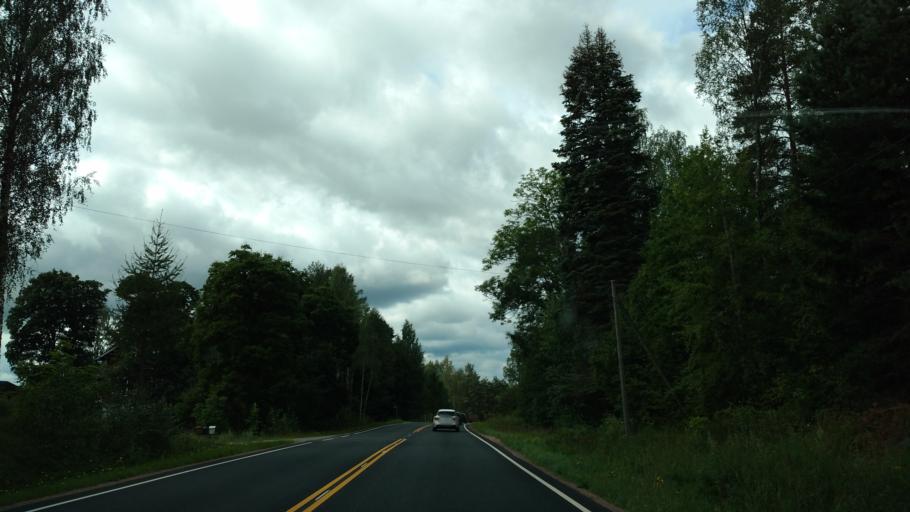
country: FI
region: Varsinais-Suomi
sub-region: Aboland-Turunmaa
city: Kimito
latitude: 60.1733
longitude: 22.8097
